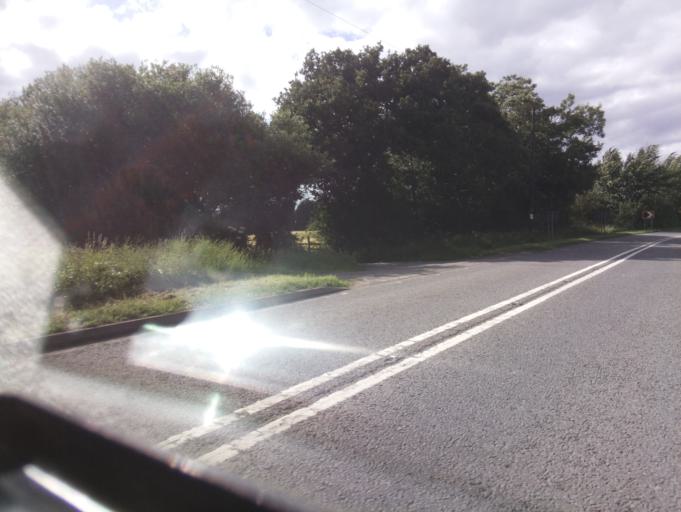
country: GB
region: England
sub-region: Warwickshire
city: Nuneaton
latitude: 52.5610
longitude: -1.4824
